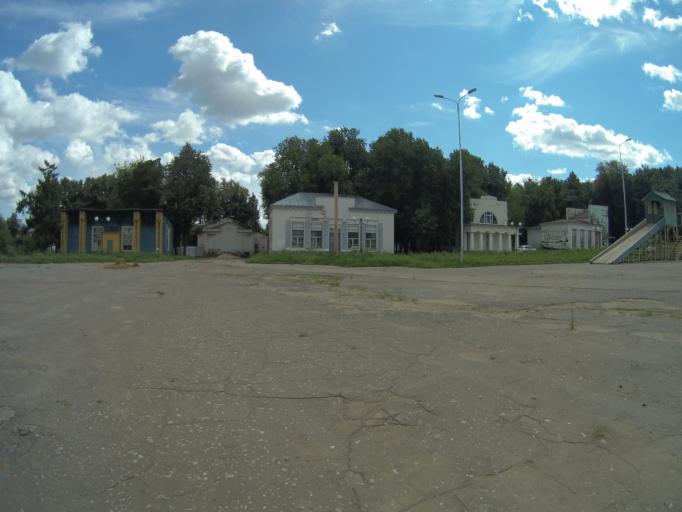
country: RU
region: Vladimir
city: Vladimir
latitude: 56.1421
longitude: 40.4155
